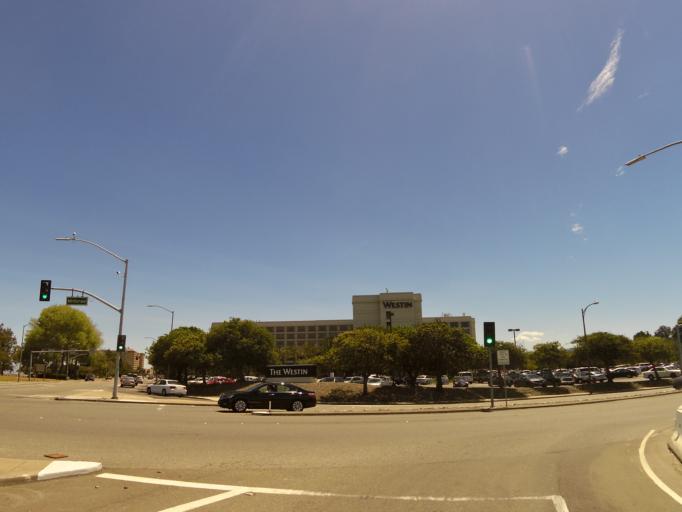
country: US
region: California
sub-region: San Mateo County
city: Millbrae
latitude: 37.6048
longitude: -122.3774
